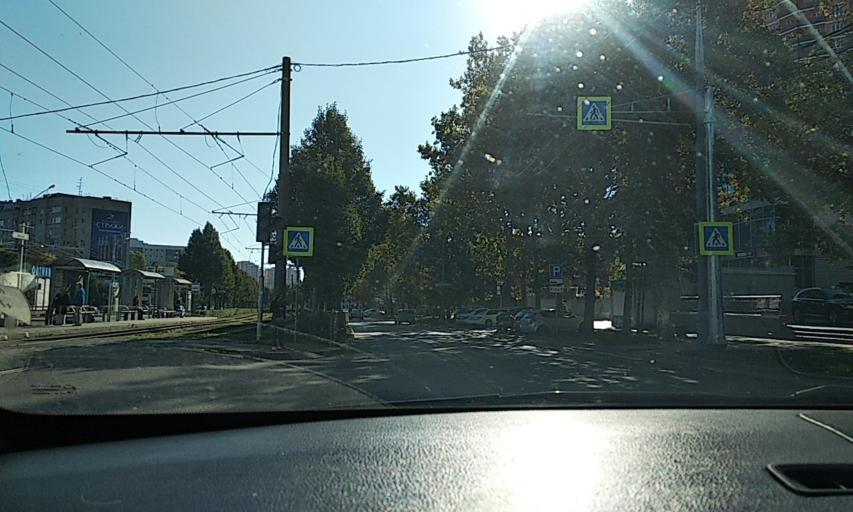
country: RU
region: Krasnodarskiy
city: Pashkovskiy
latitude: 45.0133
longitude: 39.0510
